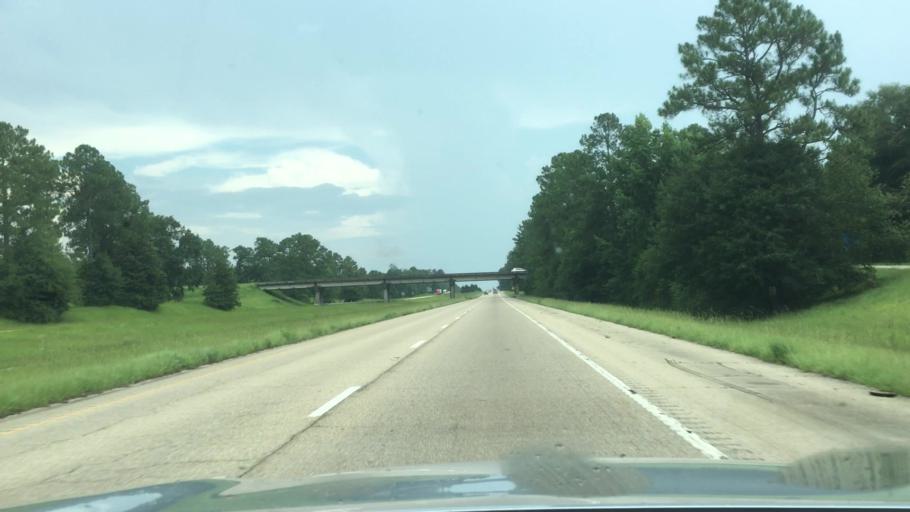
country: US
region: Mississippi
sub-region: Lamar County
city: Lumberton
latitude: 30.9988
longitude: -89.4195
